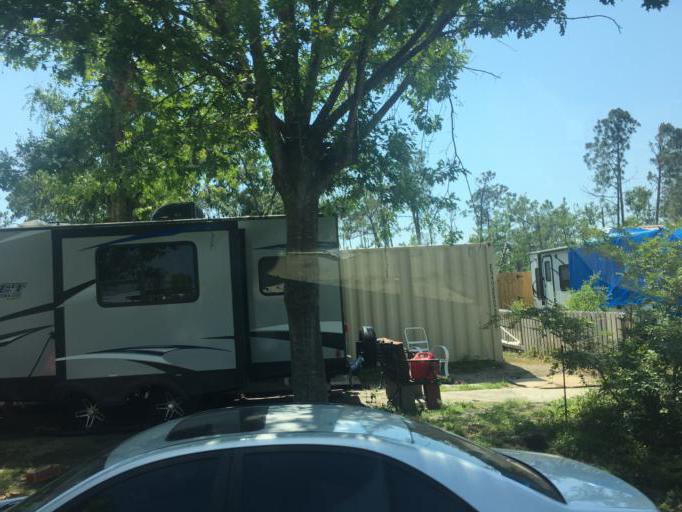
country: US
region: Florida
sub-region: Bay County
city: Lynn Haven
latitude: 30.2232
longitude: -85.6571
